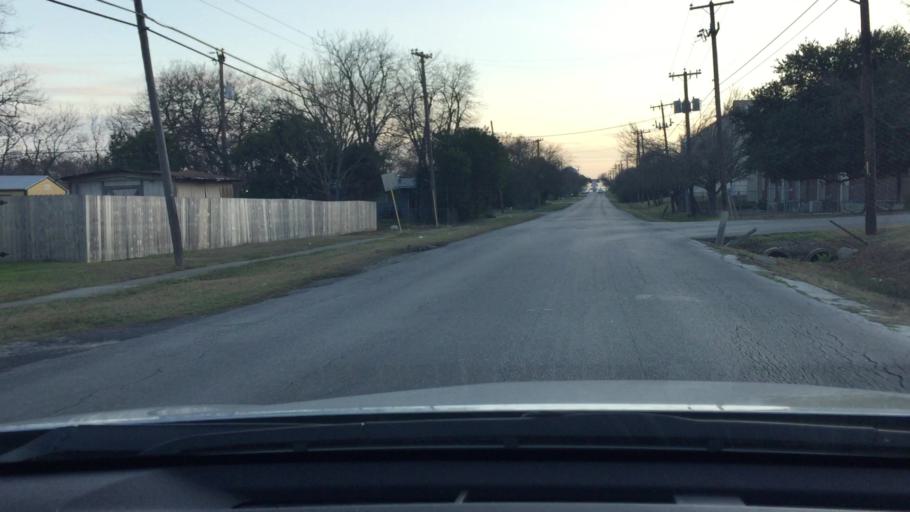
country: US
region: Texas
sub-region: Bexar County
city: Terrell Hills
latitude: 29.4919
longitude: -98.4264
